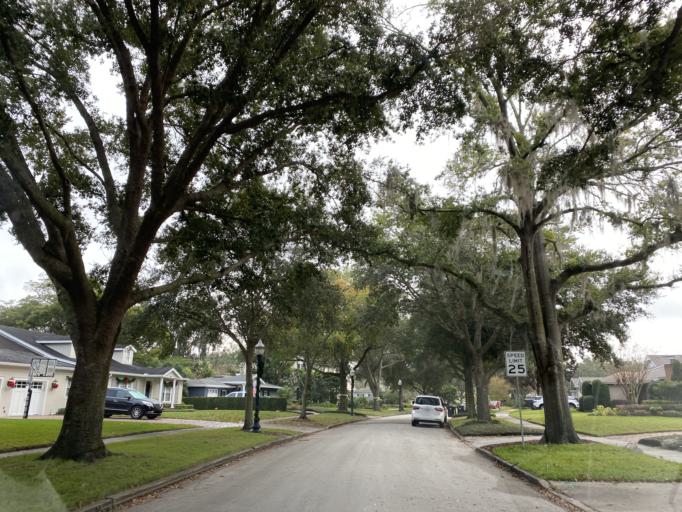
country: US
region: Florida
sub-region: Orange County
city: Fairview Shores
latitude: 28.5618
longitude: -81.3973
